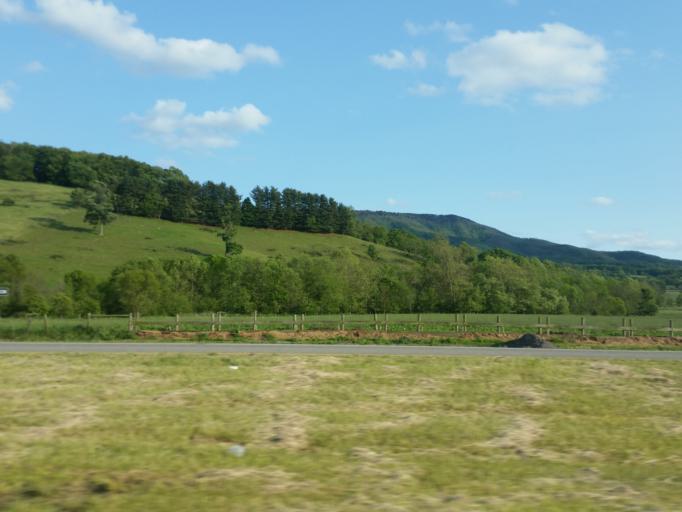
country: US
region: Virginia
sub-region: Russell County
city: Honaker
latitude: 36.9703
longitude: -81.9044
